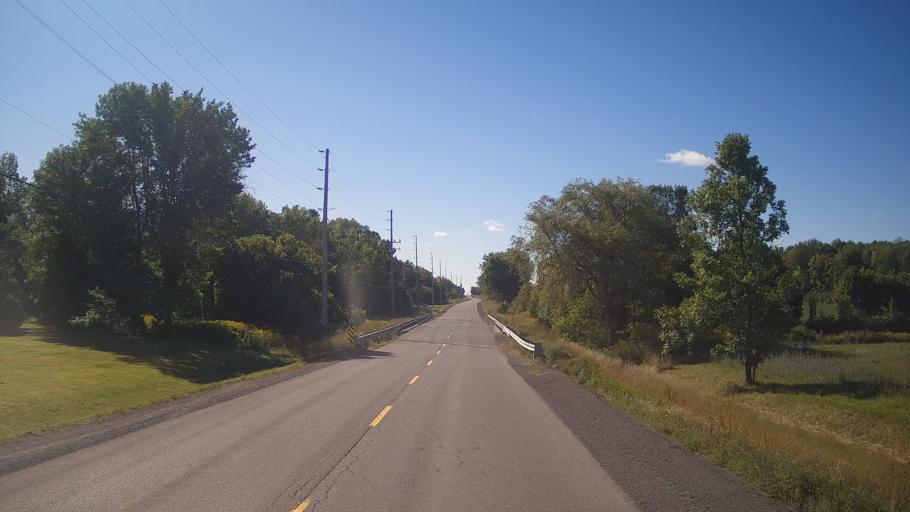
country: CA
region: Ontario
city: Prescott
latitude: 44.9807
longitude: -75.5410
